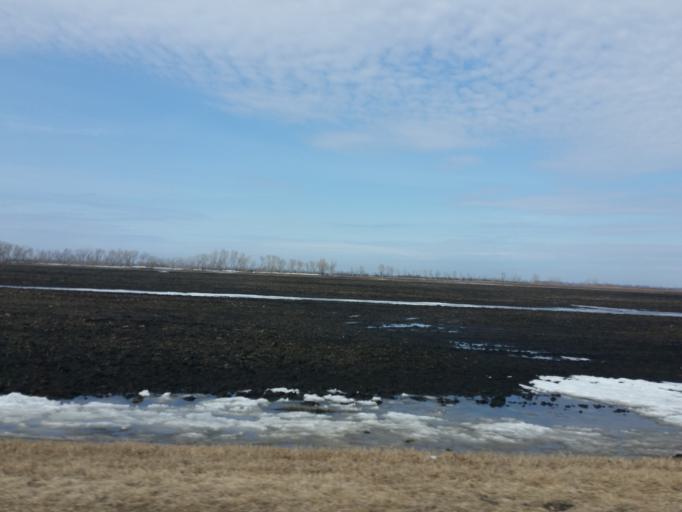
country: US
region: North Dakota
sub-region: Walsh County
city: Grafton
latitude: 48.4265
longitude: -97.2457
